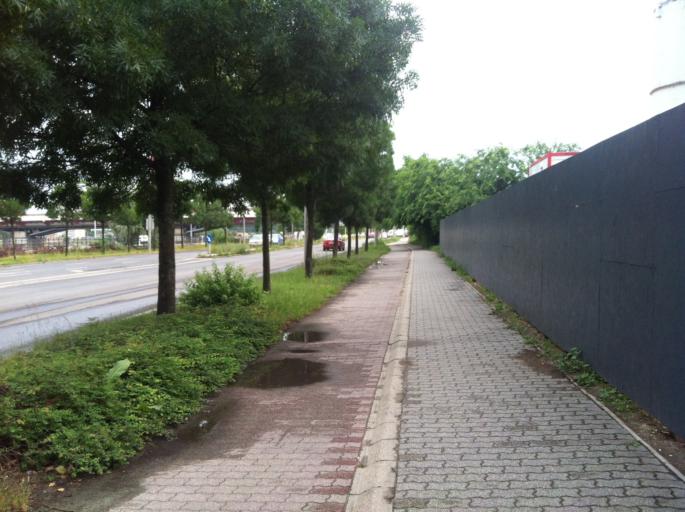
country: HU
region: Budapest
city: Budapest IX. keruelet
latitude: 47.4714
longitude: 19.0639
